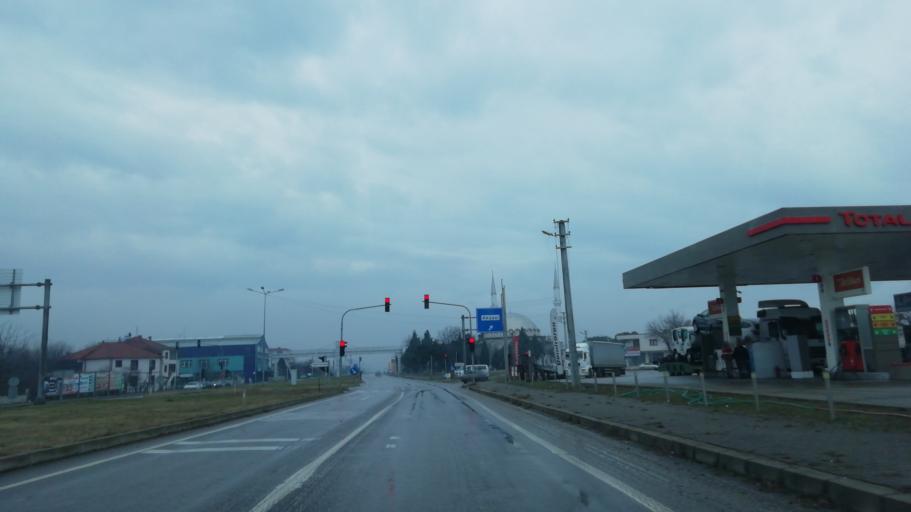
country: TR
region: Sakarya
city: Akyazi
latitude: 40.6341
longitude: 30.6291
